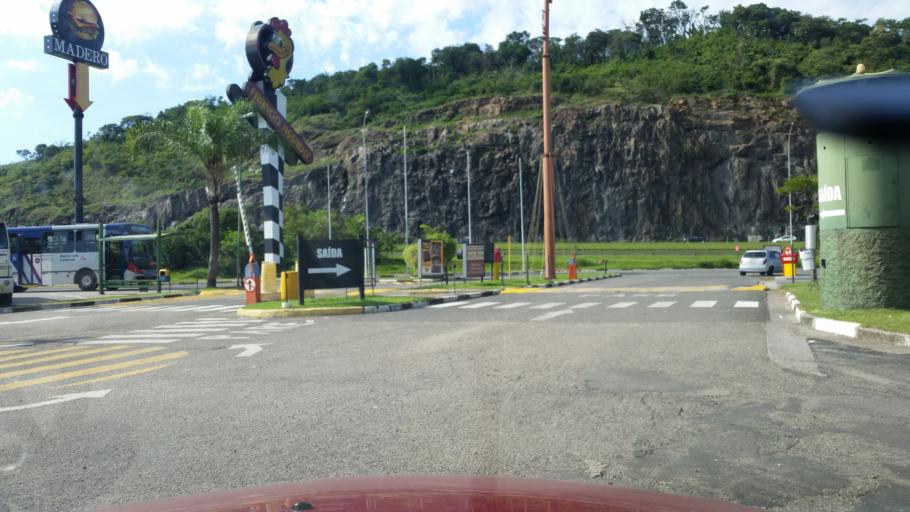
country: BR
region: Sao Paulo
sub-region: Itu
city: Itu
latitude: -23.4089
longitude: -47.2782
